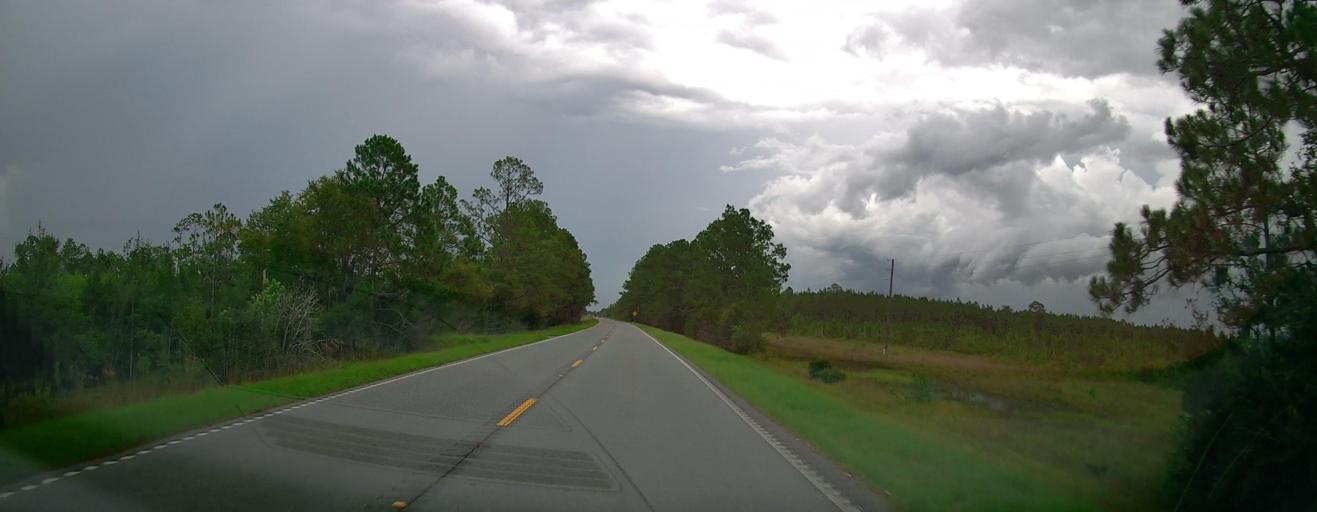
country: US
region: Georgia
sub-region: Brantley County
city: Nahunta
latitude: 31.3562
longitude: -82.0562
